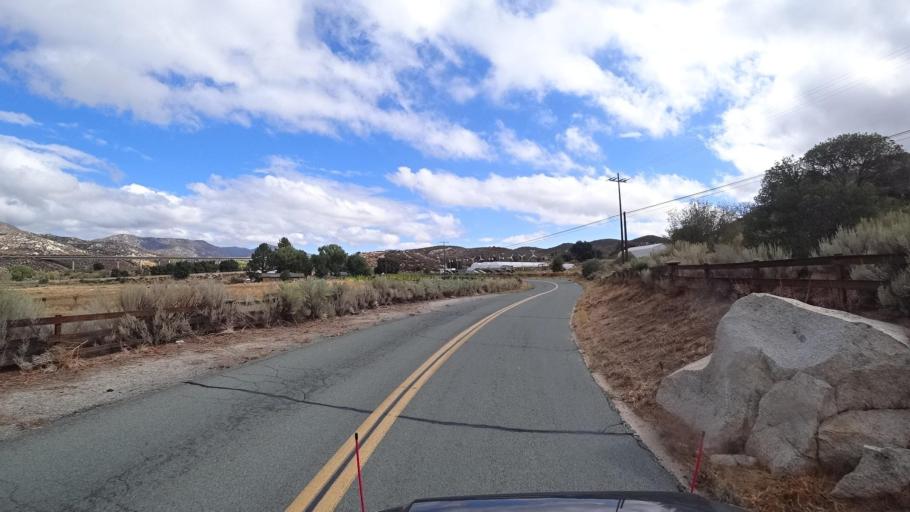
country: US
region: California
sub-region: San Diego County
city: Campo
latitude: 32.7211
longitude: -116.4284
